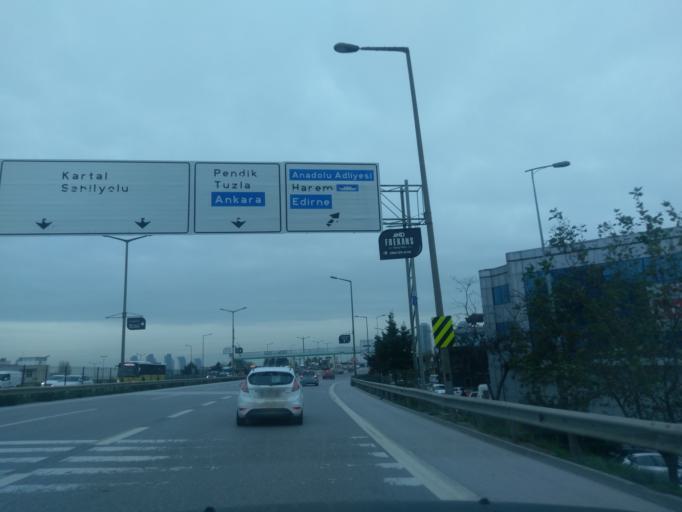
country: TR
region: Istanbul
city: Maltepe
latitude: 40.9084
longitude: 29.2128
